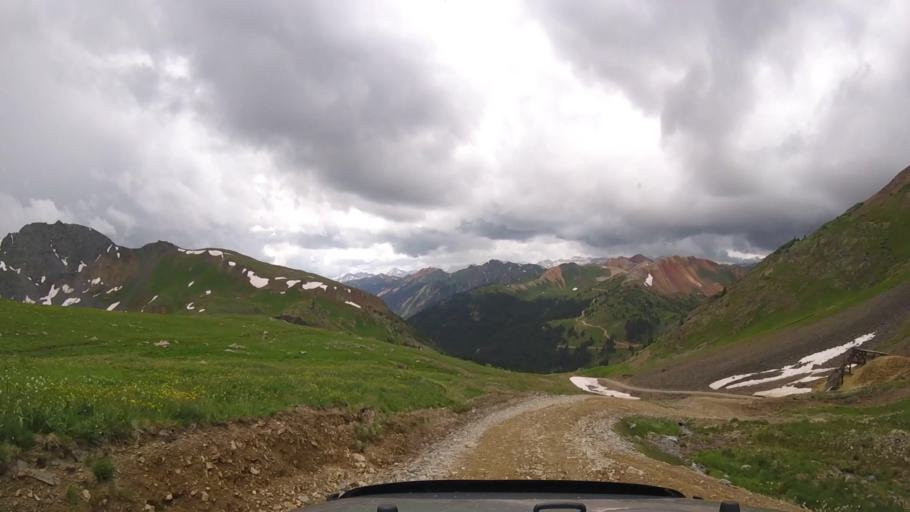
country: US
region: Colorado
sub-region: San Juan County
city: Silverton
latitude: 37.9138
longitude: -107.6292
